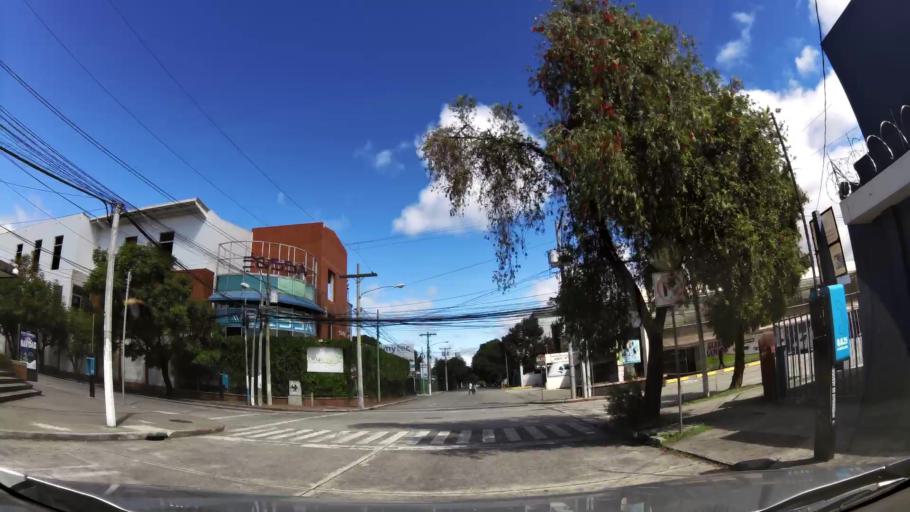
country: GT
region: Guatemala
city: Guatemala City
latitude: 14.6034
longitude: -90.5237
